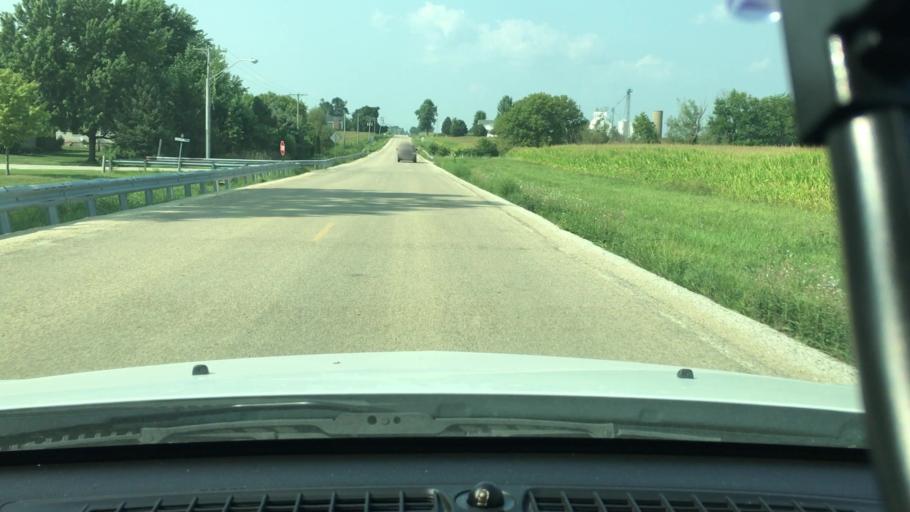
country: US
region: Illinois
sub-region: DeKalb County
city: Waterman
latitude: 41.7767
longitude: -88.7738
